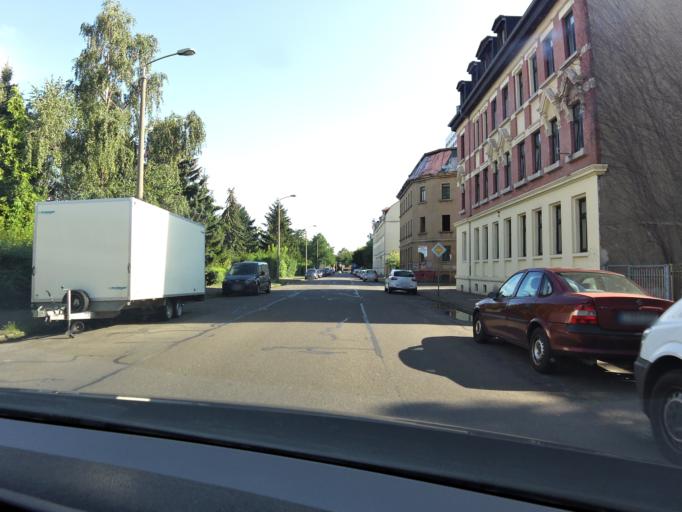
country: DE
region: Saxony
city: Taucha
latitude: 51.3816
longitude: 12.4206
